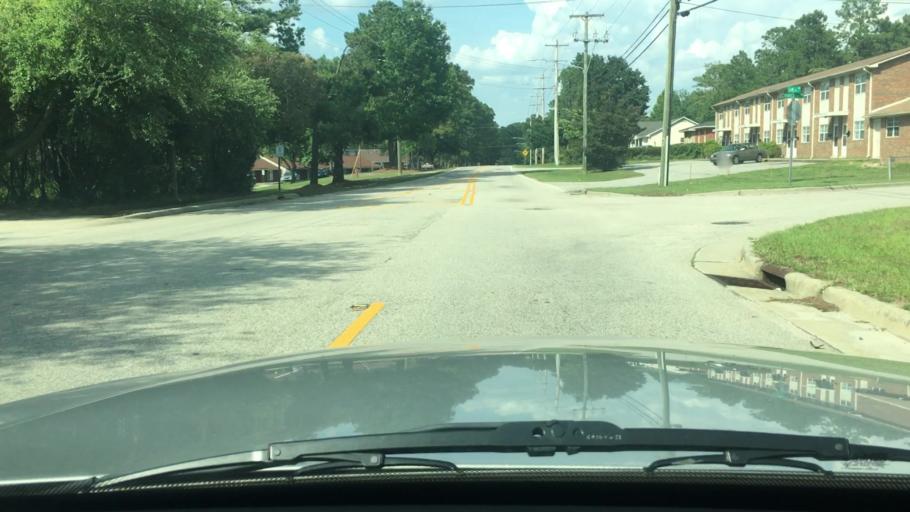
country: US
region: North Carolina
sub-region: Cumberland County
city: Fayetteville
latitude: 35.1089
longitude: -78.8765
